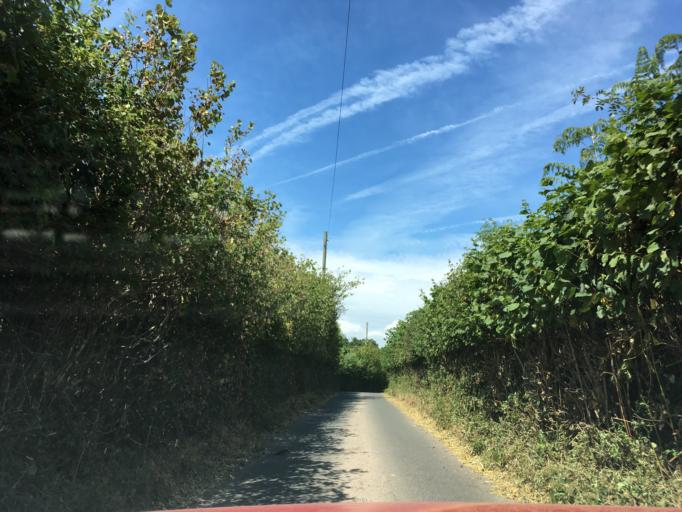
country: GB
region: Wales
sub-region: Caerphilly County Borough
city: Machen
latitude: 51.5543
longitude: -3.1443
